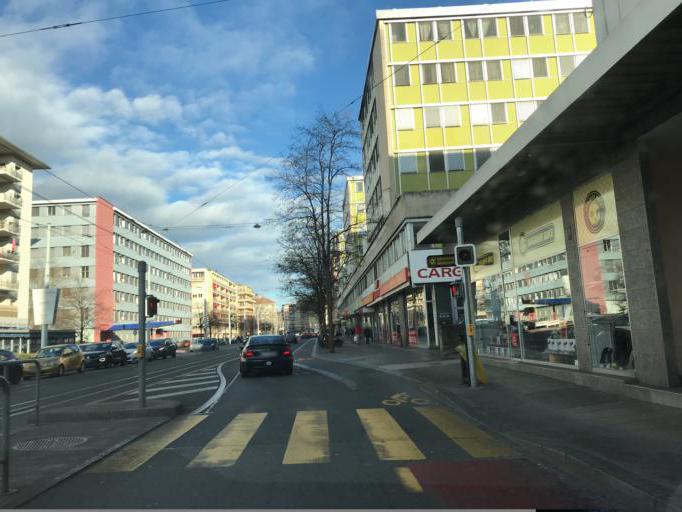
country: CH
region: Geneva
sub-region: Geneva
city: Carouge
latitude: 46.1914
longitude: 6.1360
